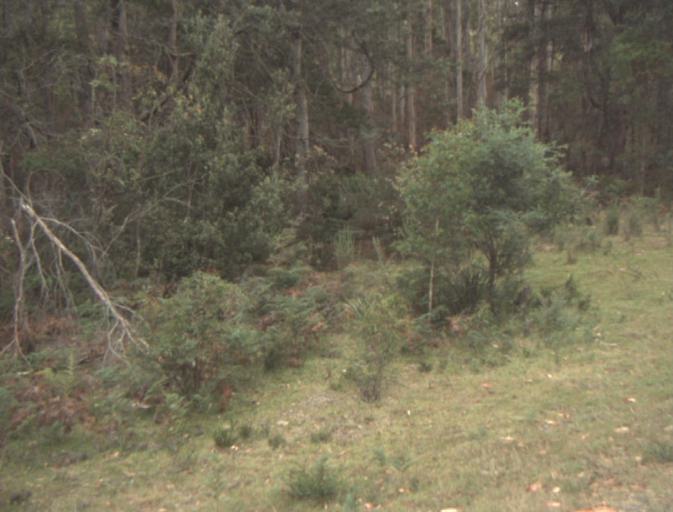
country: AU
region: Tasmania
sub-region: Dorset
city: Scottsdale
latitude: -41.4459
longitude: 147.5203
